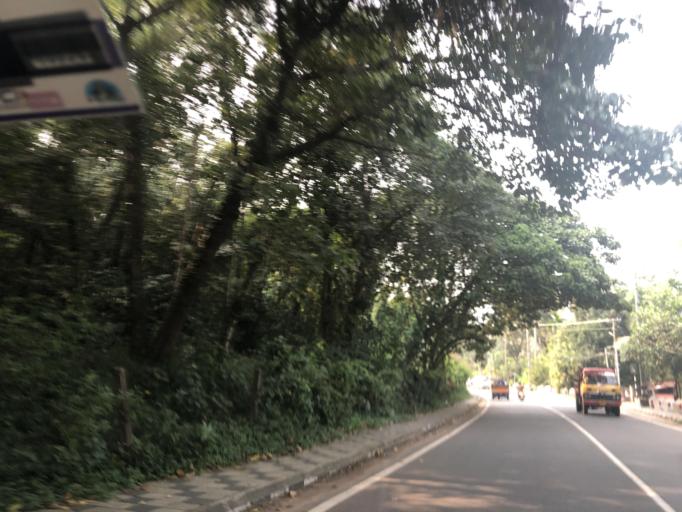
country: IN
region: Kerala
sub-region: Kozhikode
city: Kozhikode
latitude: 11.2914
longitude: 75.7709
